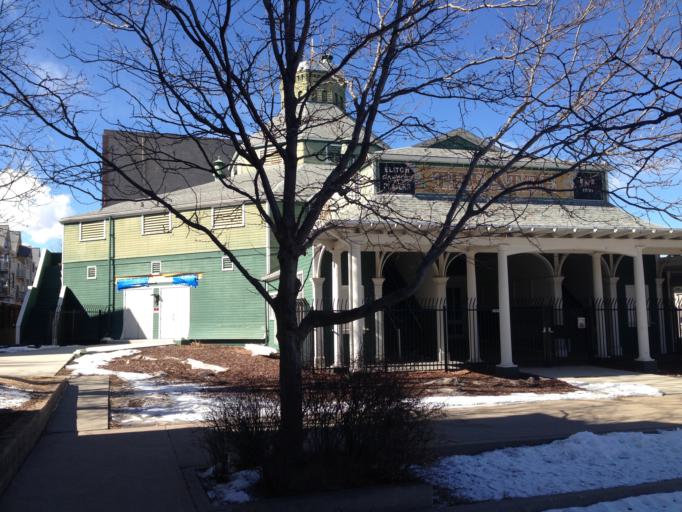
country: US
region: Colorado
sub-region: Jefferson County
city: Edgewater
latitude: 39.7681
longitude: -105.0459
